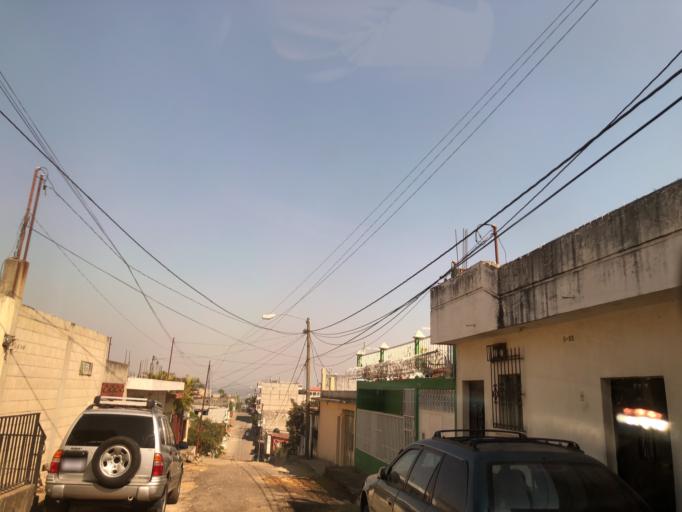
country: GT
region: Guatemala
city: Amatitlan
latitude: 14.5007
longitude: -90.5972
